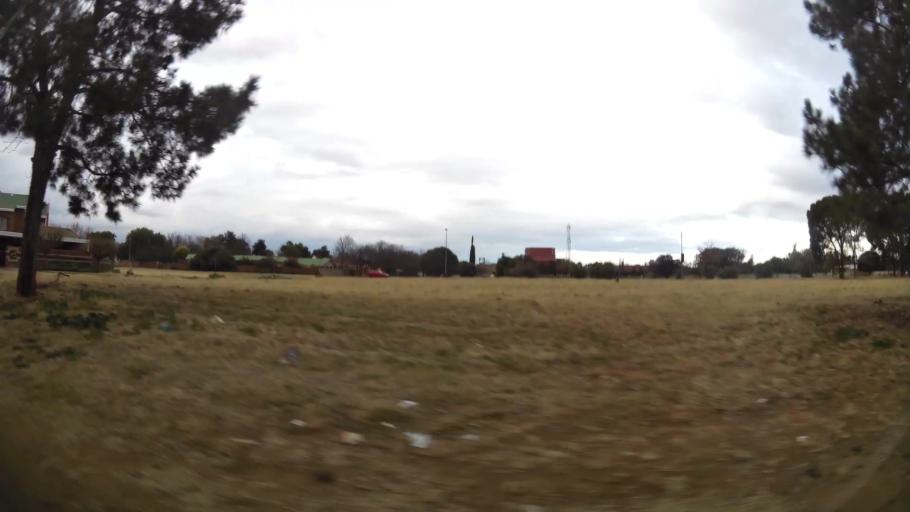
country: ZA
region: Orange Free State
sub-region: Lejweleputswa District Municipality
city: Welkom
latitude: -27.9658
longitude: 26.7255
